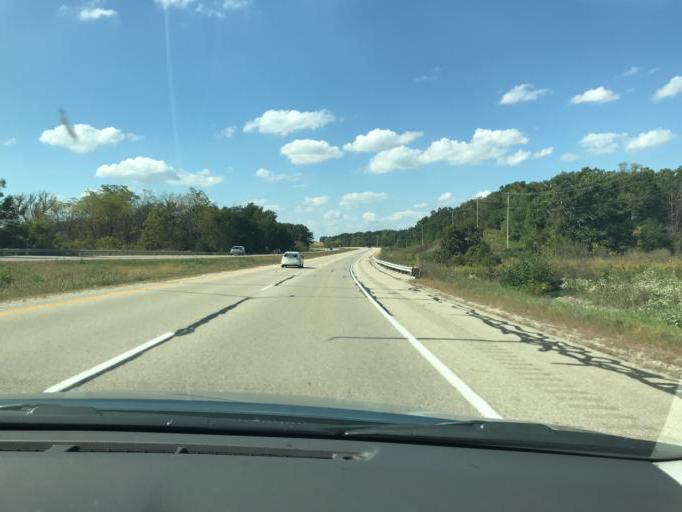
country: US
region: Wisconsin
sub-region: Walworth County
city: Pell Lake
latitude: 42.5863
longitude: -88.3386
